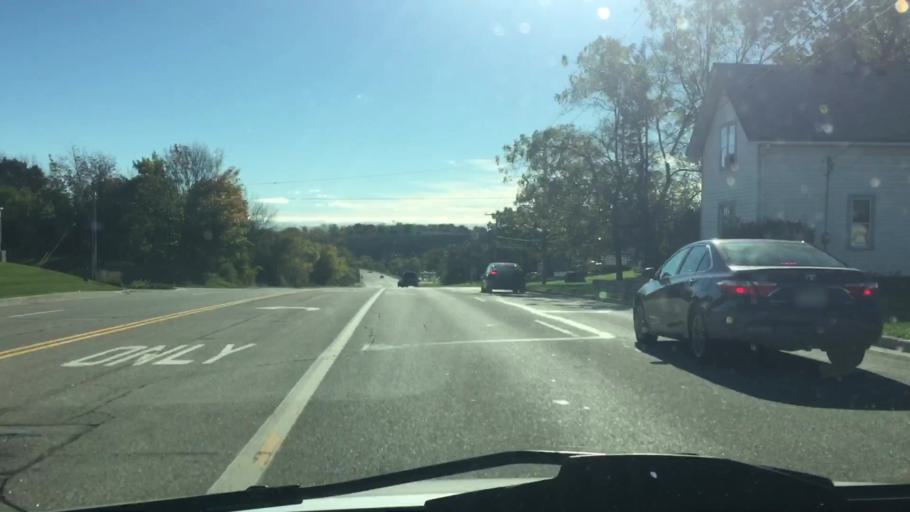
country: US
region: Wisconsin
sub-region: Waukesha County
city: Waukesha
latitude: 43.0398
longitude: -88.2207
